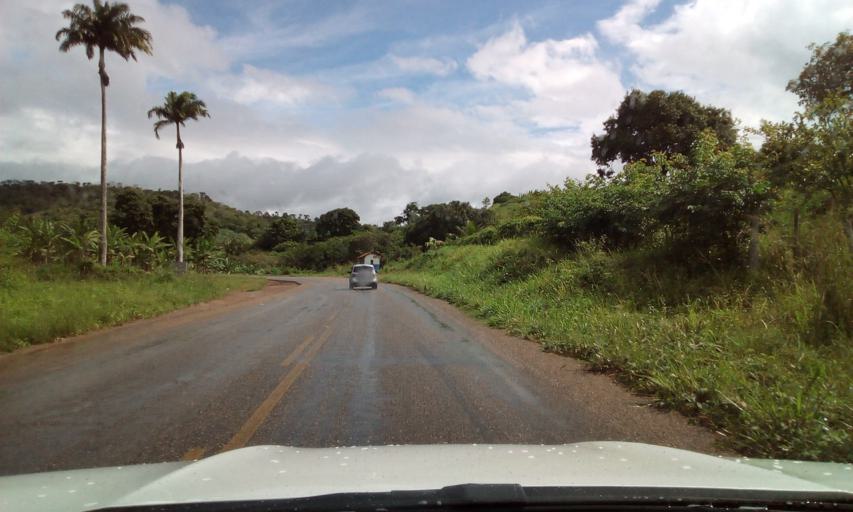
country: BR
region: Paraiba
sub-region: Areia
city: Areia
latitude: -6.9358
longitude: -35.6596
